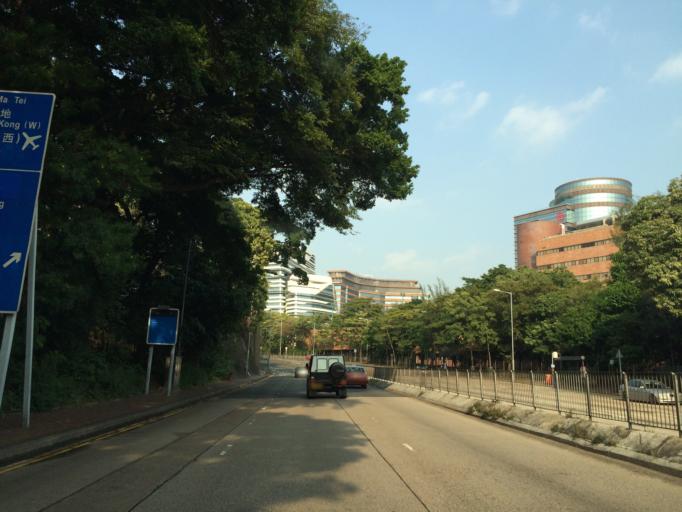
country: HK
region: Kowloon City
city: Kowloon
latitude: 22.3032
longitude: 114.1772
